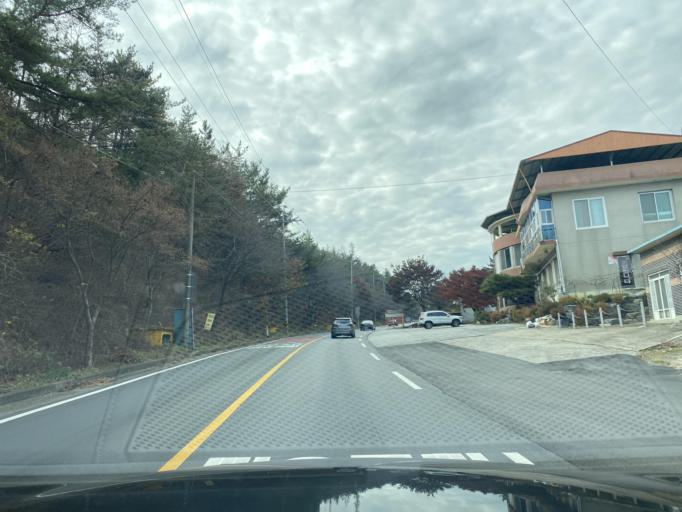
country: KR
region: Chungcheongnam-do
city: Hongsung
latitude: 36.6712
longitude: 126.6415
